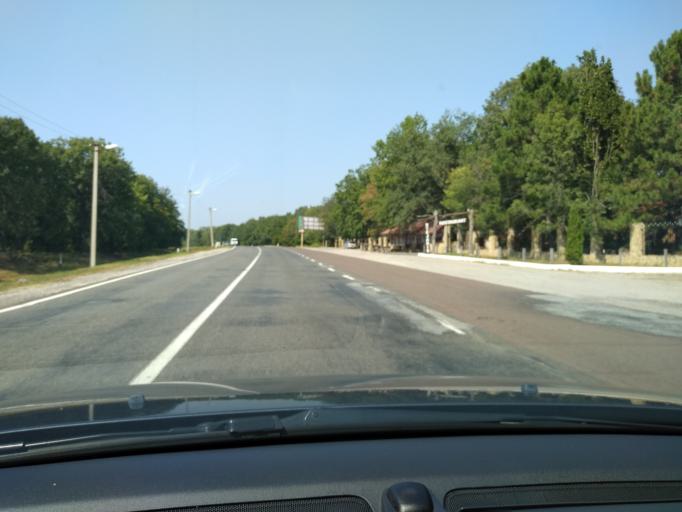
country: MD
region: Straseni
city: Straseni
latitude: 47.0277
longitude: 28.6073
